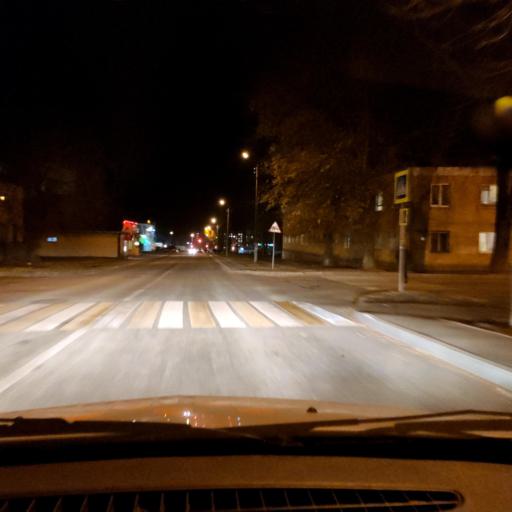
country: RU
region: Bashkortostan
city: Ufa
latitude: 54.8154
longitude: 56.1204
